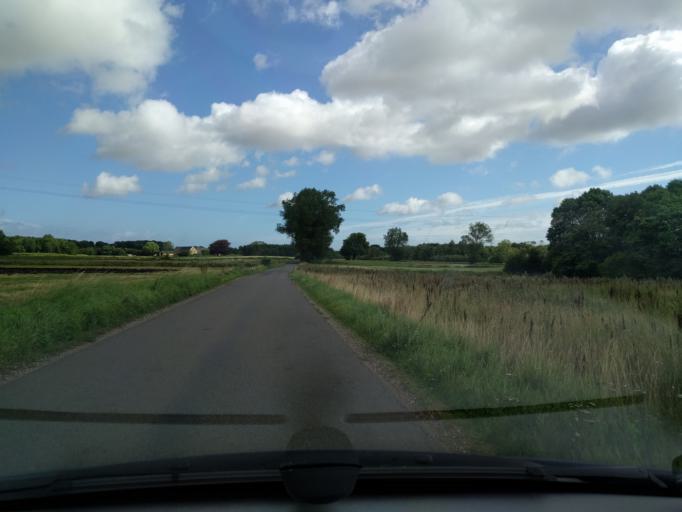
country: DK
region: South Denmark
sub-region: Kerteminde Kommune
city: Langeskov
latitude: 55.3831
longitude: 10.5783
